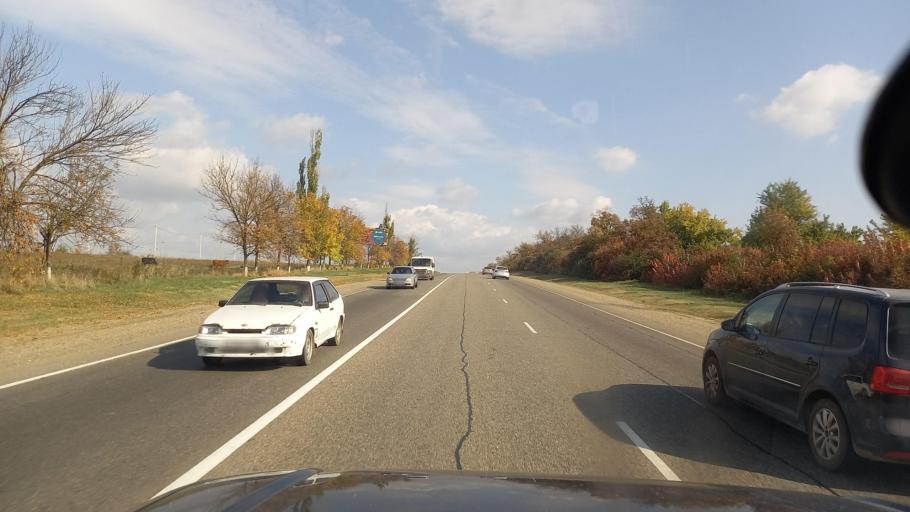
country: RU
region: Krasnodarskiy
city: Akhtyrskiy
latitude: 44.8459
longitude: 38.3116
